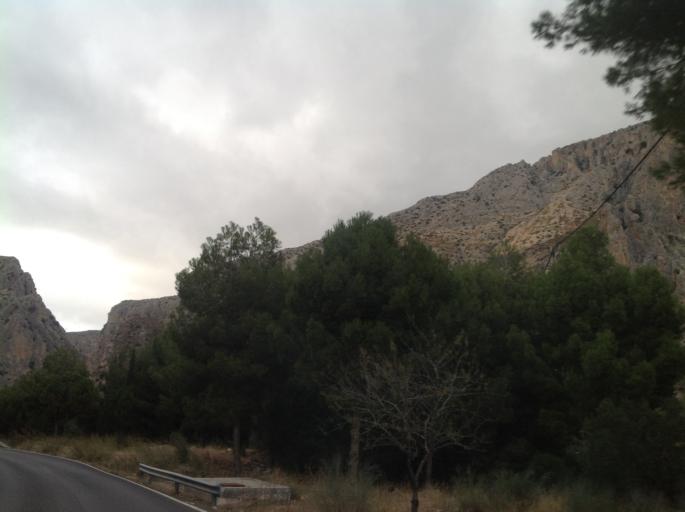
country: ES
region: Andalusia
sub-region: Provincia de Malaga
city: Carratraca
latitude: 36.9095
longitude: -4.7641
